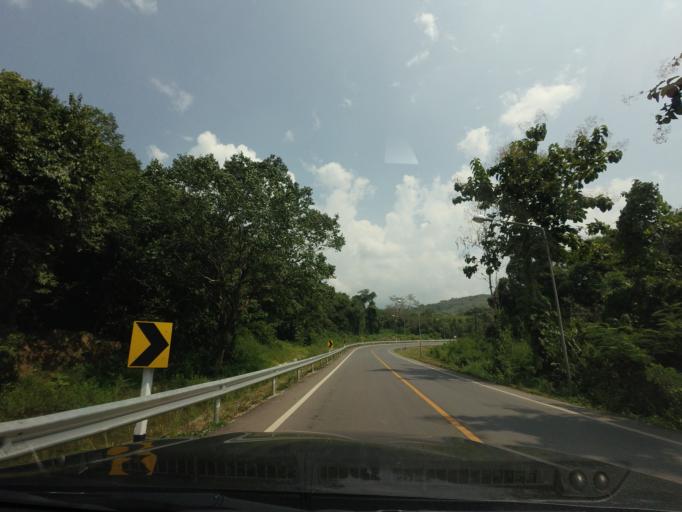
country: TH
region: Nan
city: Santi Suk
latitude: 18.9865
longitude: 100.9354
